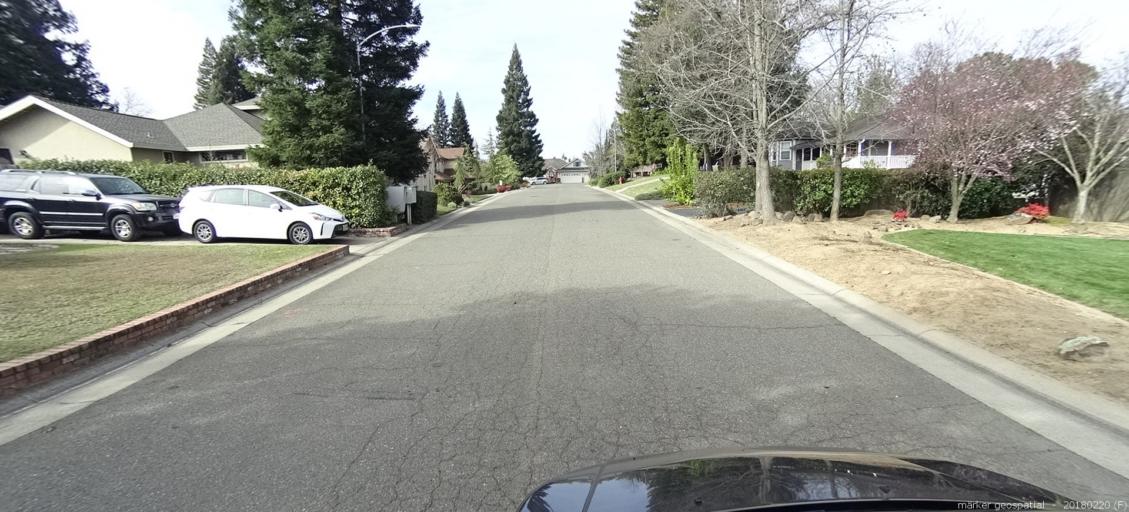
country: US
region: California
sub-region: Sacramento County
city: Orangevale
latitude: 38.6917
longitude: -121.2305
